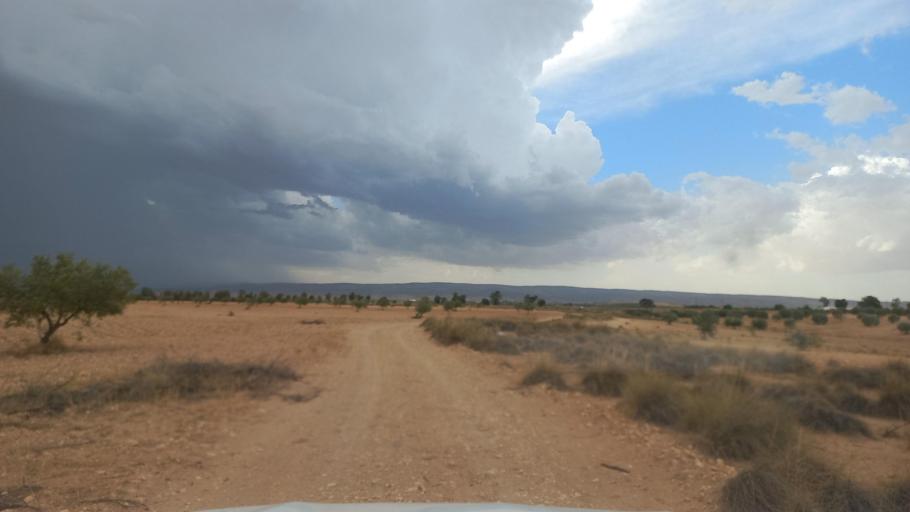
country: TN
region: Al Qasrayn
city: Kasserine
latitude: 35.2447
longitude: 9.0073
